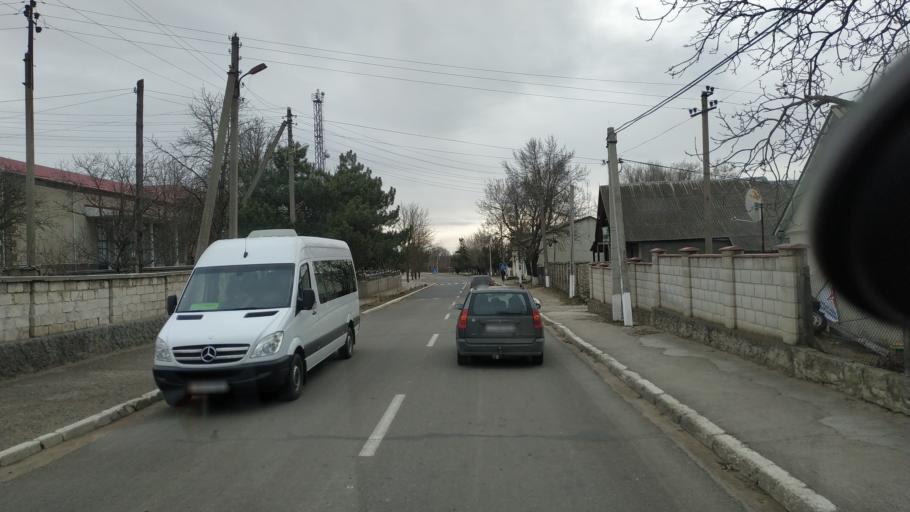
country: MD
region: Telenesti
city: Cocieri
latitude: 47.3100
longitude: 29.1077
